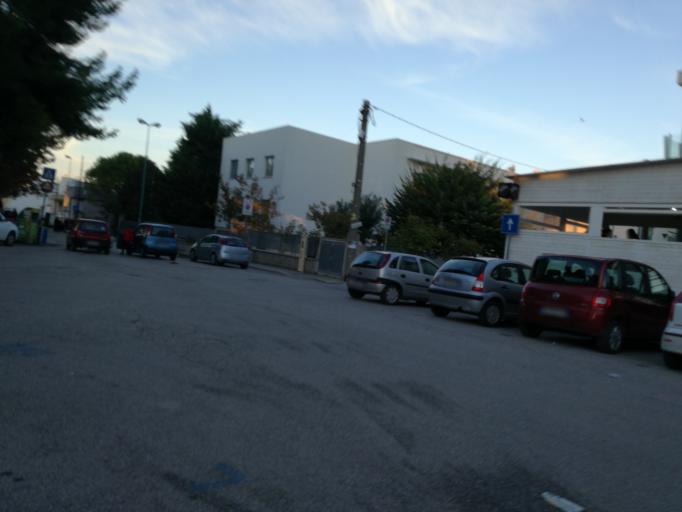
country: IT
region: Apulia
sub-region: Provincia di Bari
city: Adelfia
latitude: 41.0008
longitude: 16.8762
